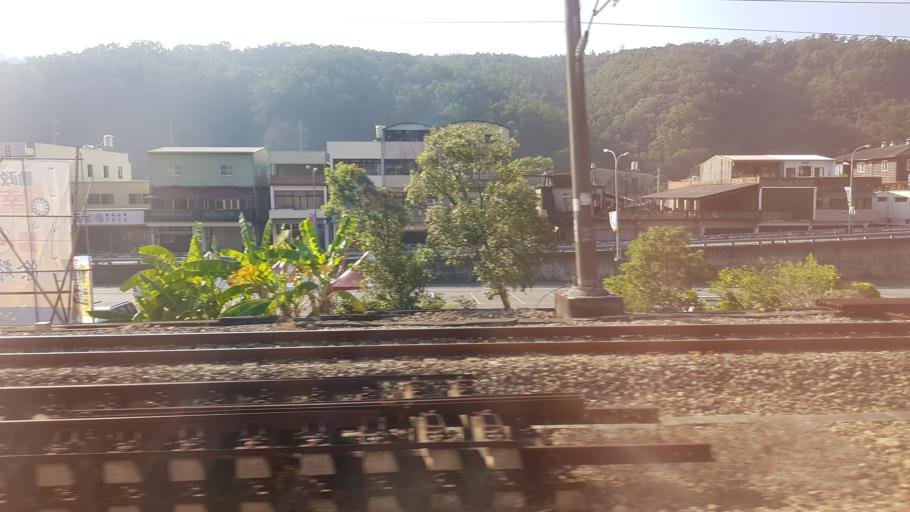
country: TW
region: Taiwan
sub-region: Miaoli
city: Miaoli
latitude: 24.4219
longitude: 120.7743
